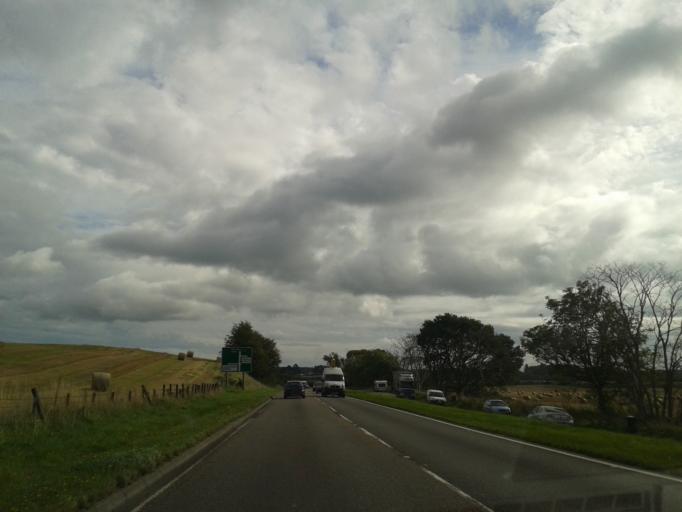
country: GB
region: Scotland
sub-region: Moray
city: Lhanbryd
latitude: 57.6397
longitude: -3.2573
